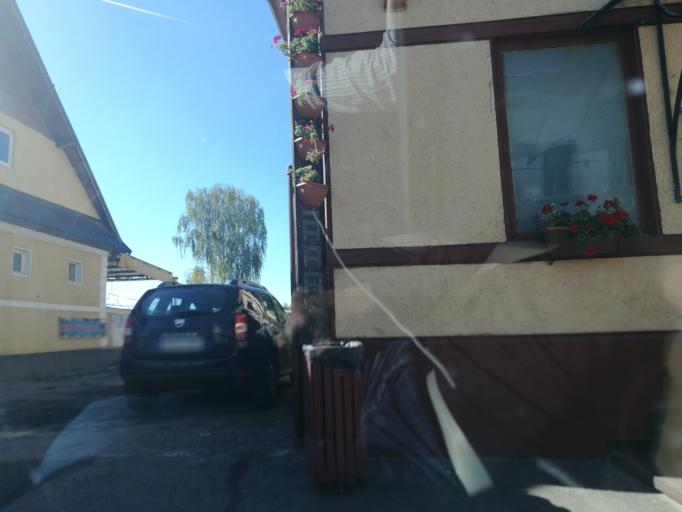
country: RO
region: Brasov
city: Fogarasch
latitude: 45.8402
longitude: 24.9737
